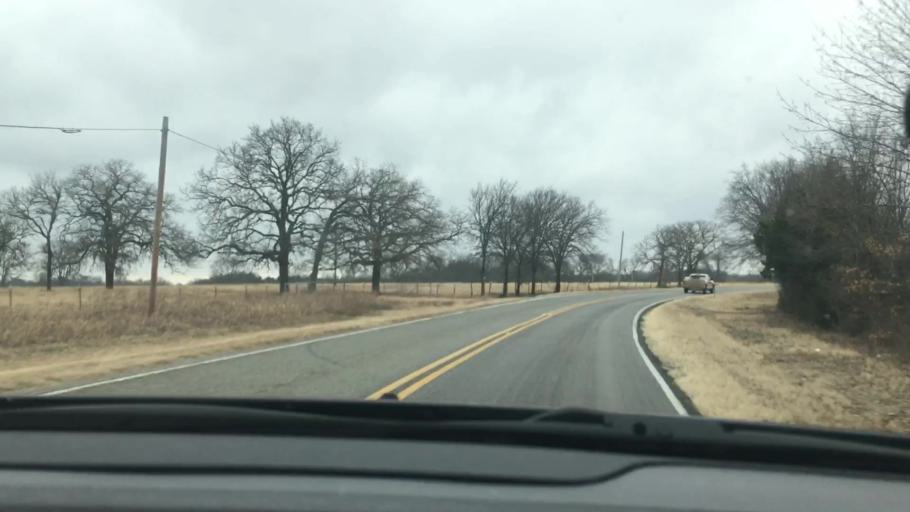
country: US
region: Oklahoma
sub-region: Johnston County
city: Tishomingo
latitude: 34.1858
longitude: -96.5795
